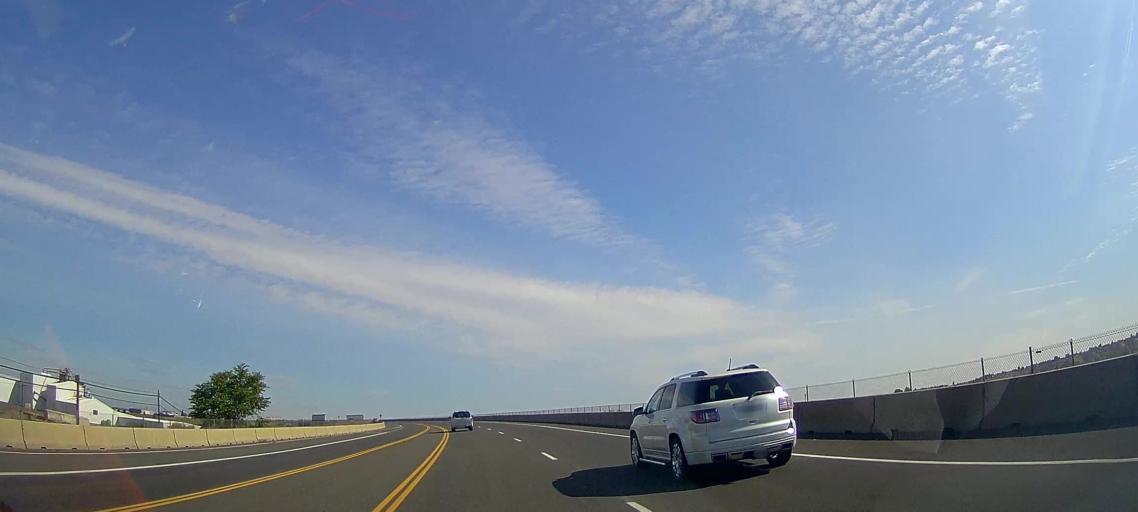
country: US
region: Oregon
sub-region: Jefferson County
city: Madras
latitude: 44.6534
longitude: -121.1289
